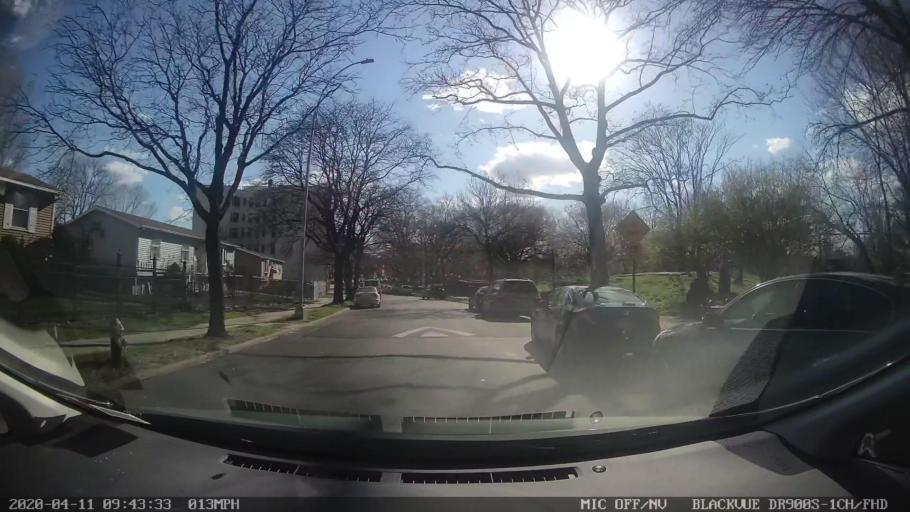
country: US
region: New York
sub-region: Bronx
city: The Bronx
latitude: 40.8362
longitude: -73.8942
